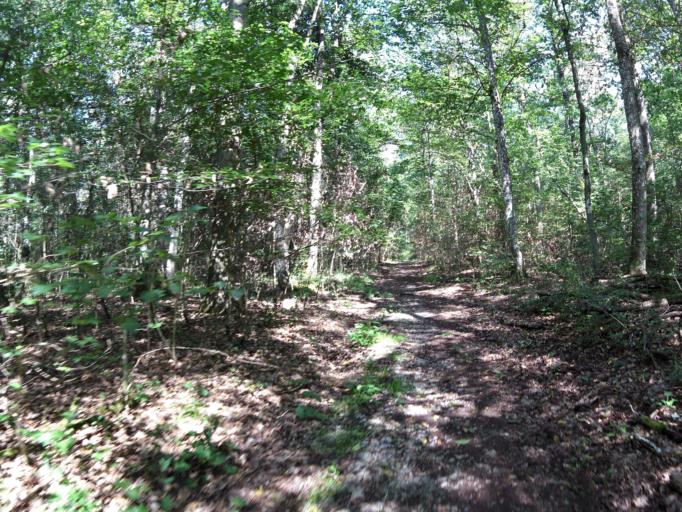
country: DE
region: Bavaria
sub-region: Regierungsbezirk Unterfranken
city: Margetshochheim
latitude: 49.8581
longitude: 9.8692
